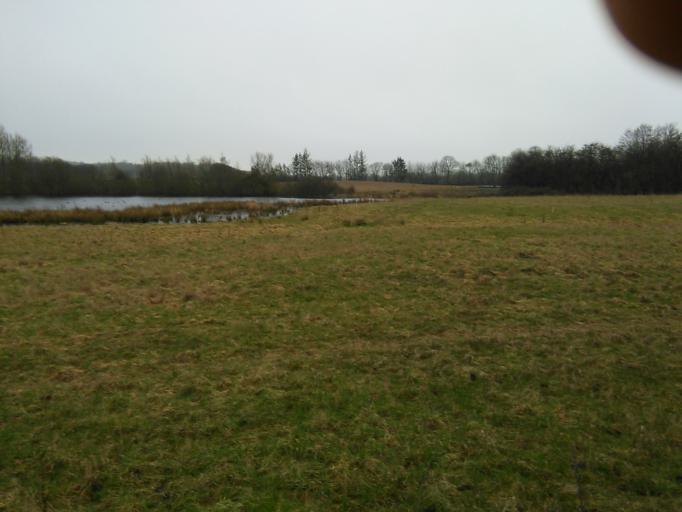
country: DK
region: Central Jutland
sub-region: Arhus Kommune
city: Beder
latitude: 56.0528
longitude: 10.2119
